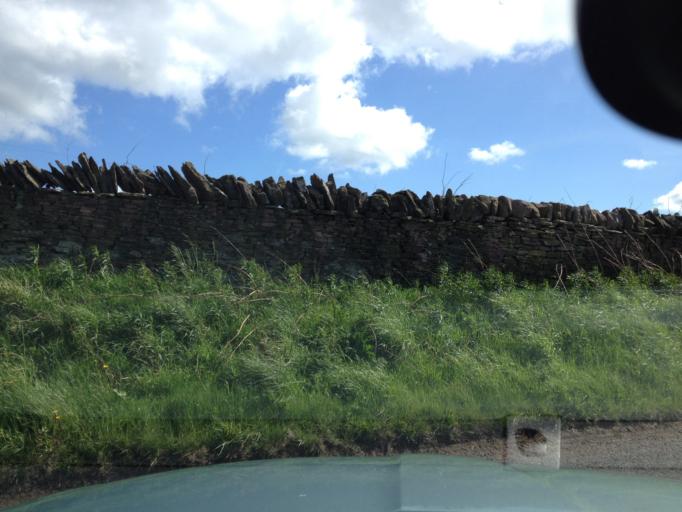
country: GB
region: Scotland
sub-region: Angus
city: Letham
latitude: 56.7005
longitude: -2.7629
